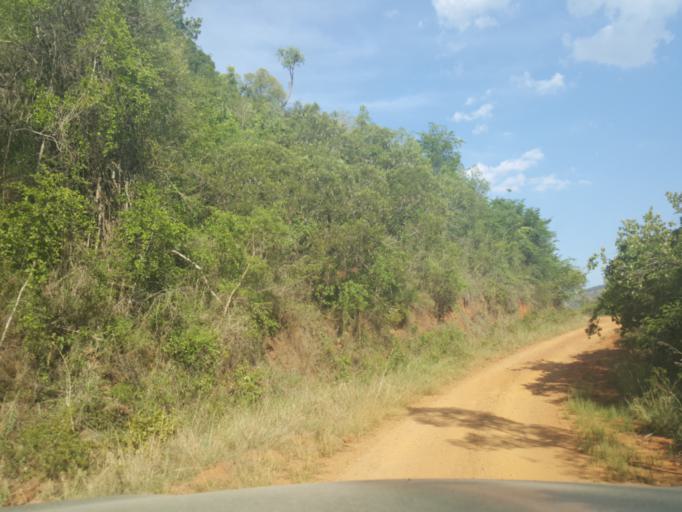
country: ZA
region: Limpopo
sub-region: Mopani District Municipality
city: Hoedspruit
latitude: -24.5931
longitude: 30.8309
